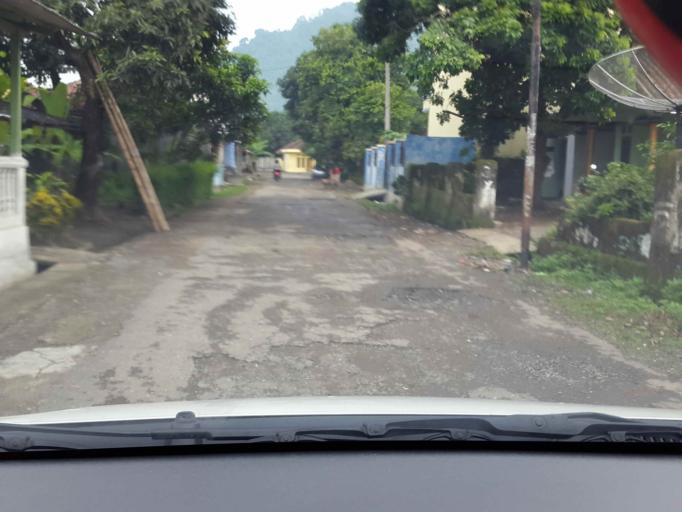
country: ID
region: West Java
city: Cidadap
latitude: -7.0197
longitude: 106.5585
